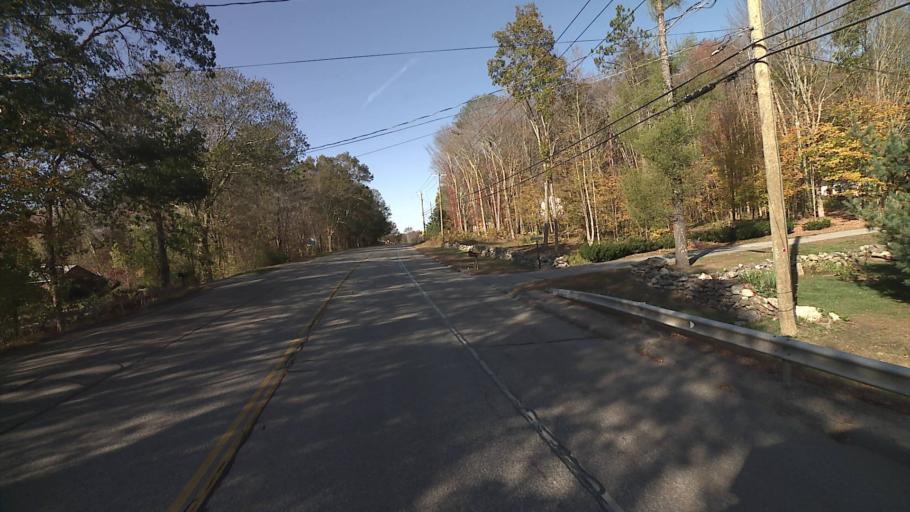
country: US
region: Connecticut
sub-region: Windham County
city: Windham
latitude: 41.7672
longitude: -72.1060
